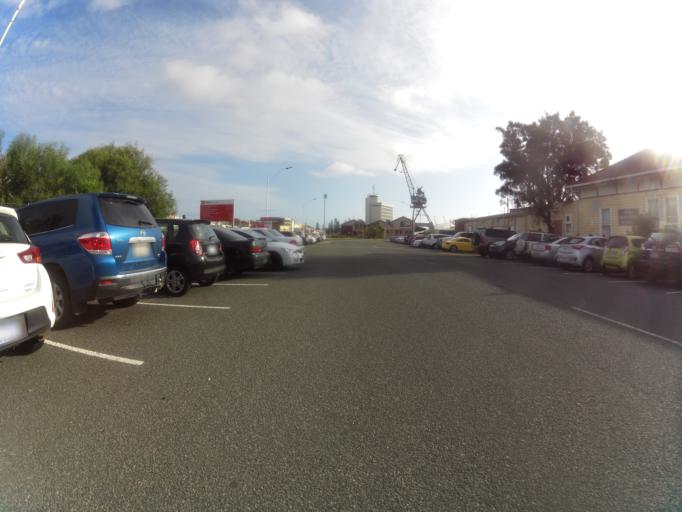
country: AU
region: Western Australia
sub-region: Fremantle
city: North Fremantle
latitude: -32.0521
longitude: 115.7442
